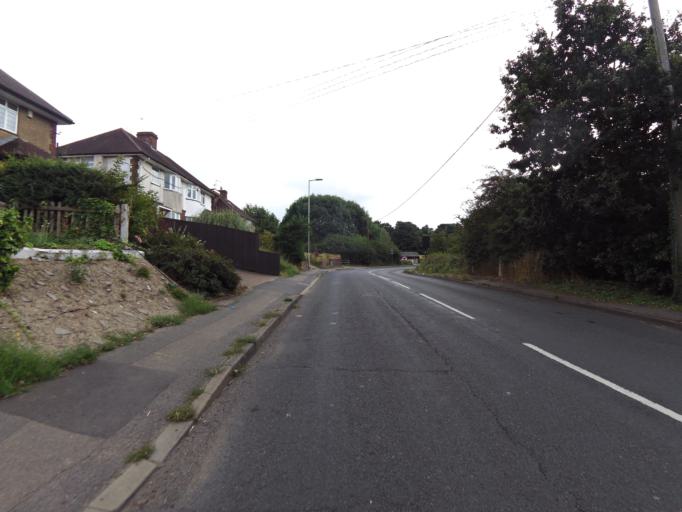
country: GB
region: England
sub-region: Hertfordshire
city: Shenley AV
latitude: 51.7173
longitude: -0.3001
